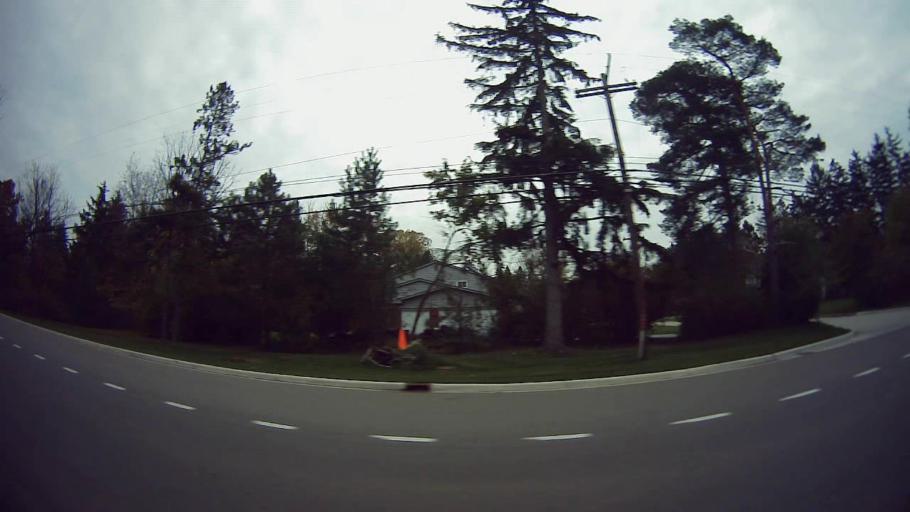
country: US
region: Michigan
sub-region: Oakland County
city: Bingham Farms
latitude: 42.5266
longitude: -83.2639
